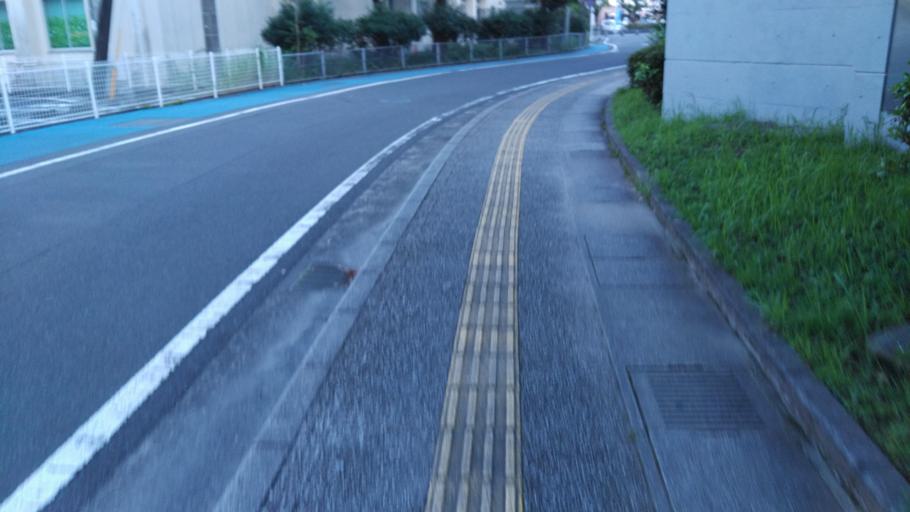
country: JP
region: Kagoshima
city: Kokubu-matsuki
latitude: 31.7408
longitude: 130.7639
